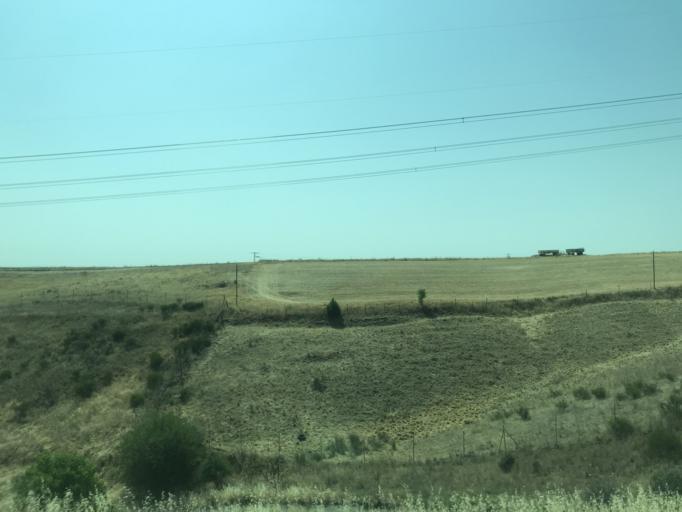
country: ES
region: Madrid
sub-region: Provincia de Madrid
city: El Molar
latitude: 40.7299
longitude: -3.5709
